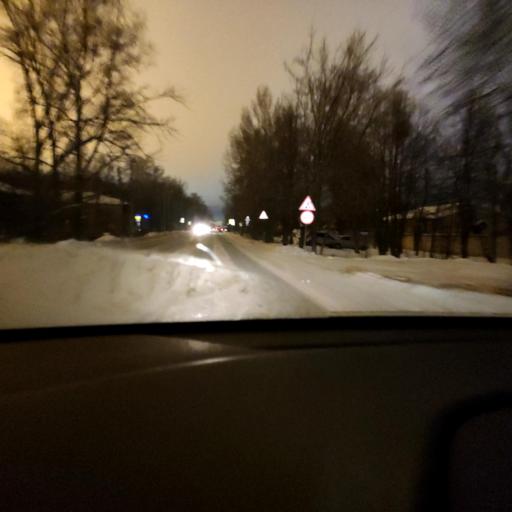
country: RU
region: Tatarstan
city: Osinovo
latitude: 55.8802
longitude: 48.8859
